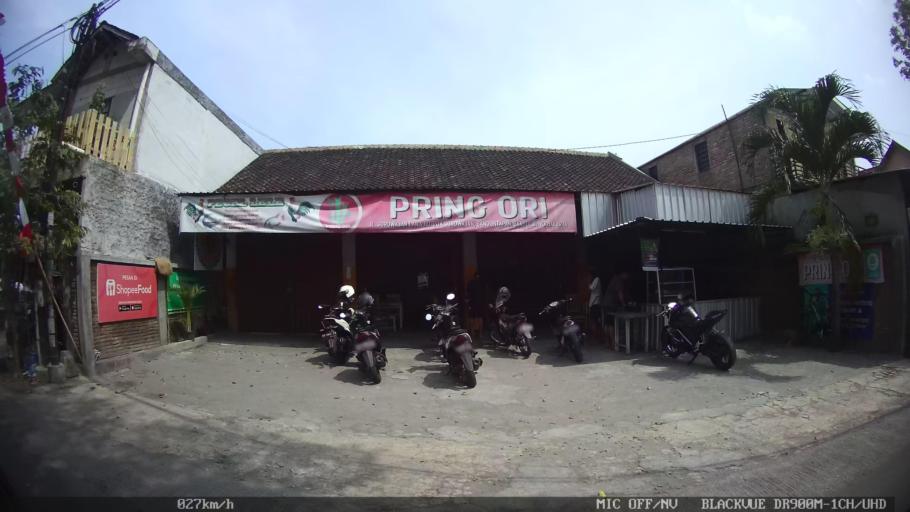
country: ID
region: Daerah Istimewa Yogyakarta
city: Depok
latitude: -7.7939
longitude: 110.4065
